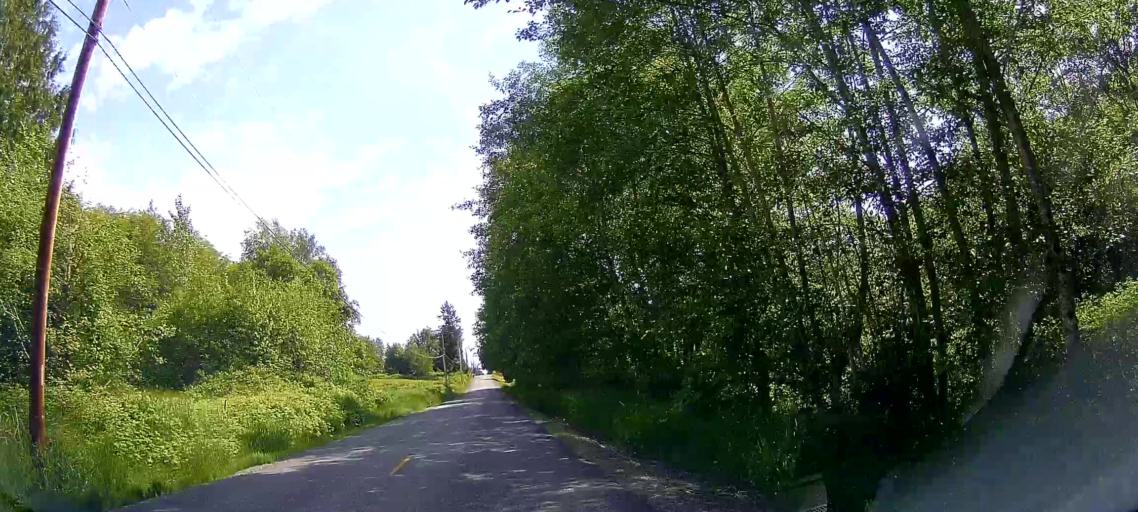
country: US
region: Washington
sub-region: Skagit County
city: Burlington
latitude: 48.5650
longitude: -122.3618
